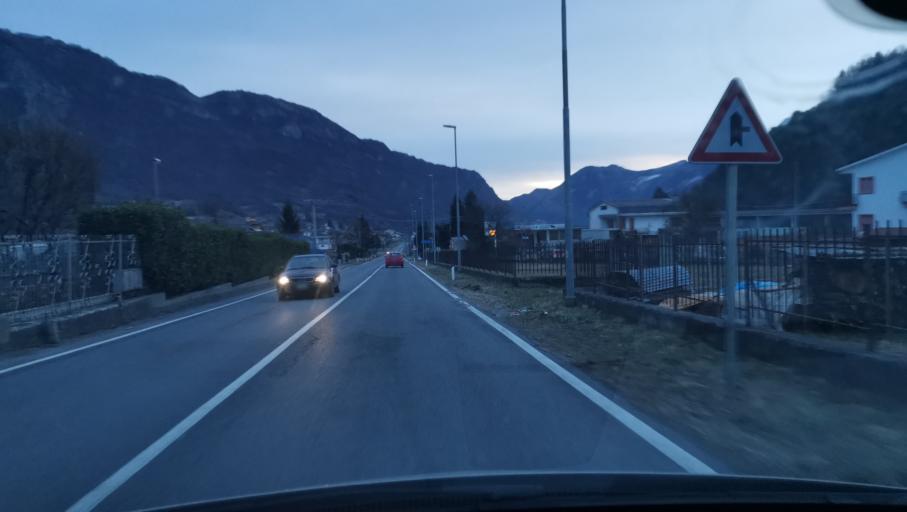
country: IT
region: Piedmont
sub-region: Provincia di Cuneo
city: Demonte
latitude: 44.3160
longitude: 7.3039
